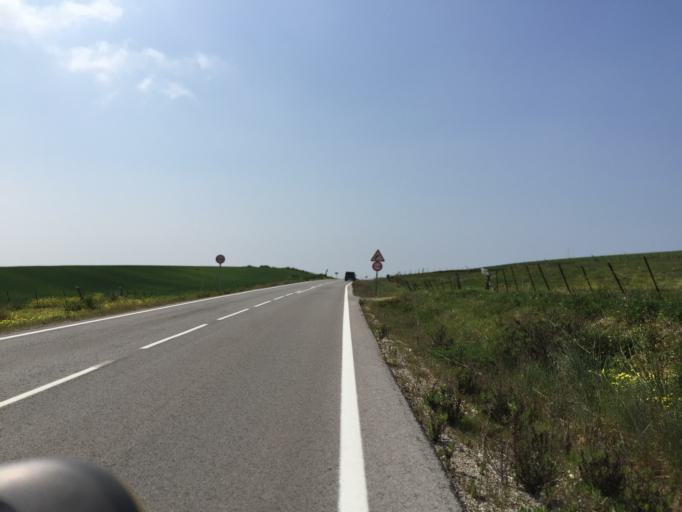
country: ES
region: Andalusia
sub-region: Provincia de Cadiz
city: Vejer de la Frontera
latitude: 36.2327
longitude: -6.0317
